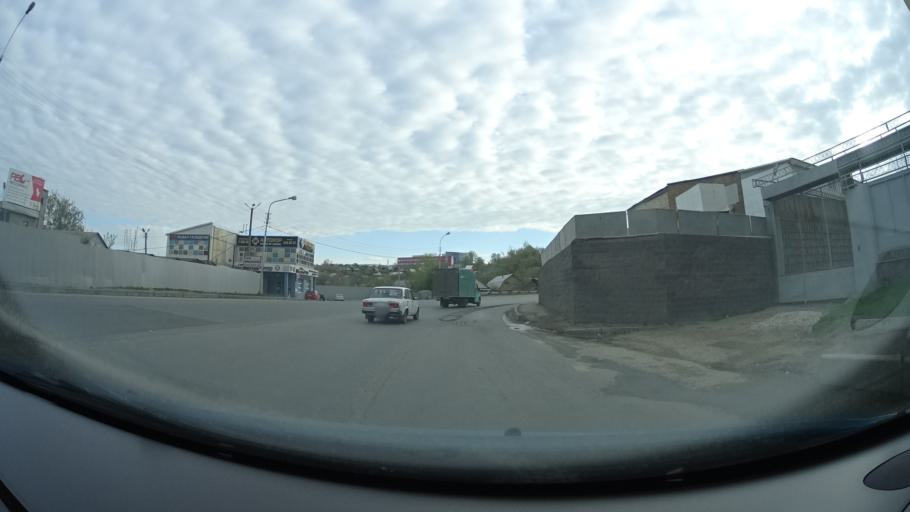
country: RU
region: Bashkortostan
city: Ufa
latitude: 54.7479
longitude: 55.9716
